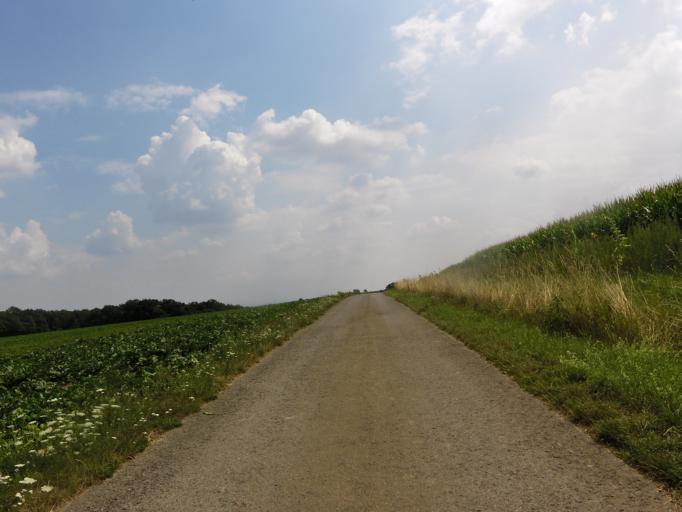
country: DE
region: Bavaria
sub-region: Regierungsbezirk Unterfranken
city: Eibelstadt
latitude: 49.7254
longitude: 9.9770
